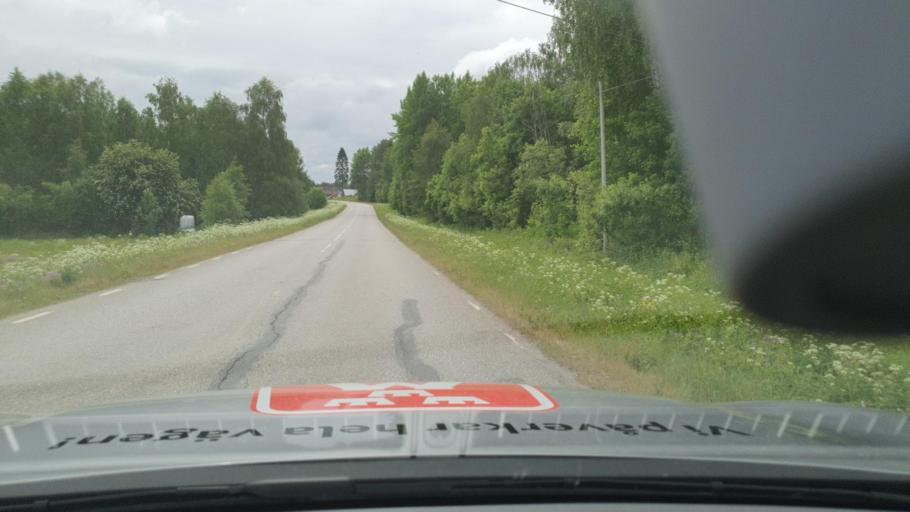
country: SE
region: Norrbotten
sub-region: Lulea Kommun
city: Ranea
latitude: 65.9212
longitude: 22.1491
